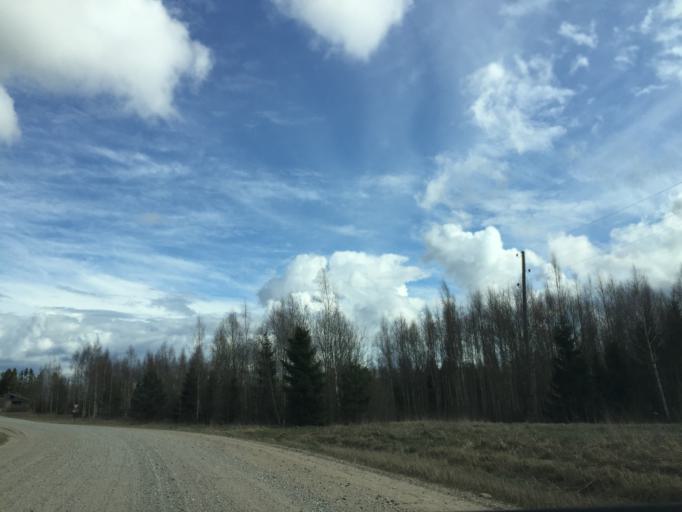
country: LV
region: Limbazu Rajons
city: Limbazi
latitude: 57.6030
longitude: 24.8013
